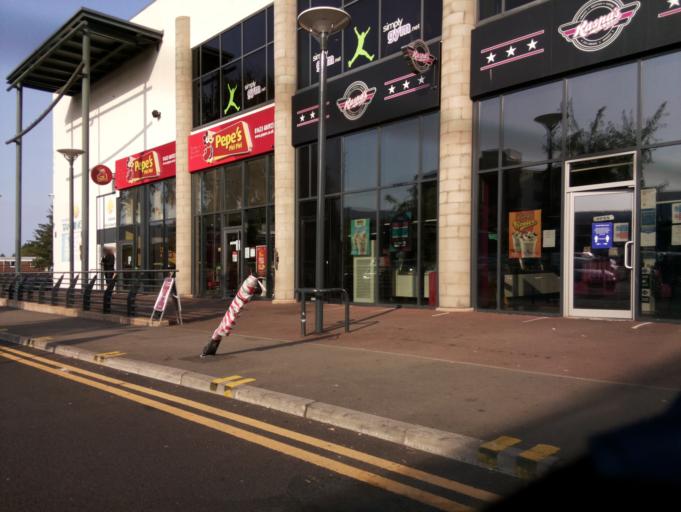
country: GB
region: Wales
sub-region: Torfaen County Borough
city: Cwmbran
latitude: 51.6546
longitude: -3.0202
